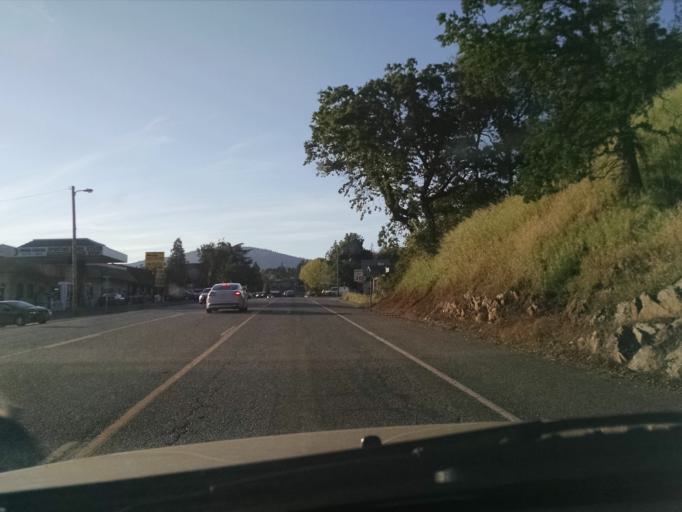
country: US
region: California
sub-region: Mariposa County
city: Mariposa
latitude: 37.4881
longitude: -119.9687
